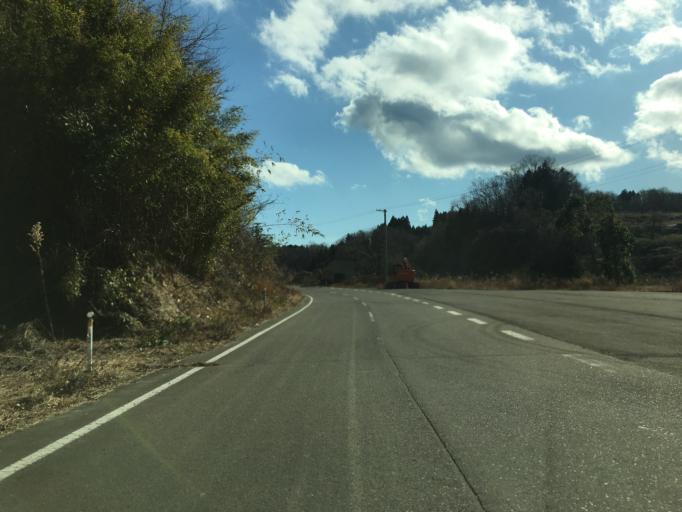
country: JP
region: Fukushima
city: Funehikimachi-funehiki
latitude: 37.4159
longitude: 140.5571
